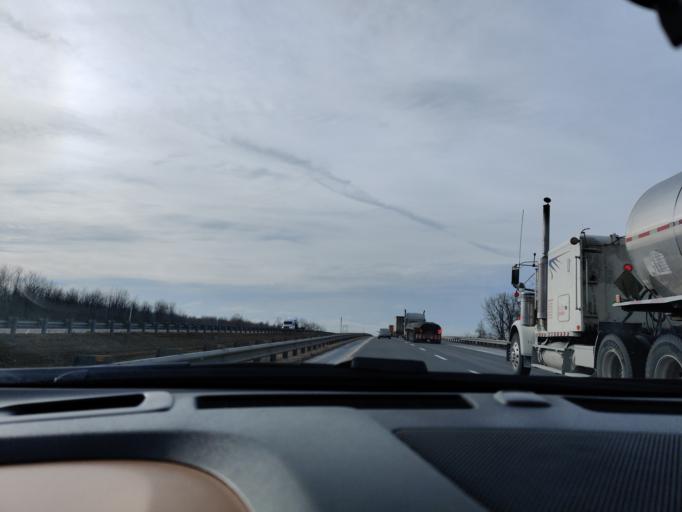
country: CA
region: Quebec
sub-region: Monteregie
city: Les Coteaux
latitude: 45.2726
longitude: -74.2144
